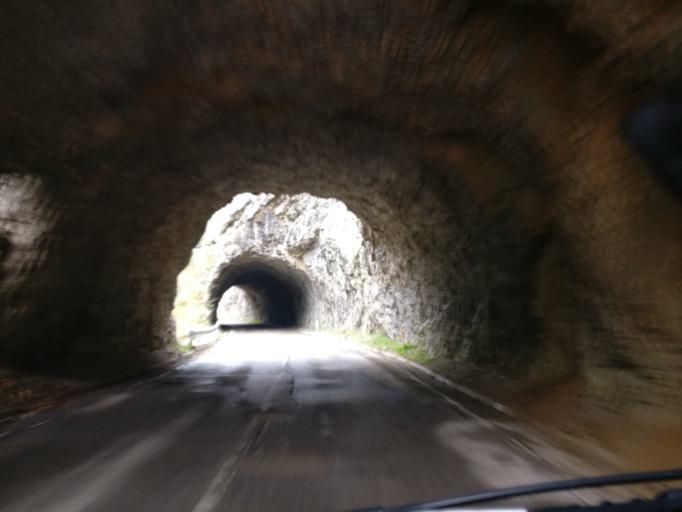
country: ME
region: Opstina Pluzine
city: Pluzine
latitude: 43.2873
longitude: 18.8496
